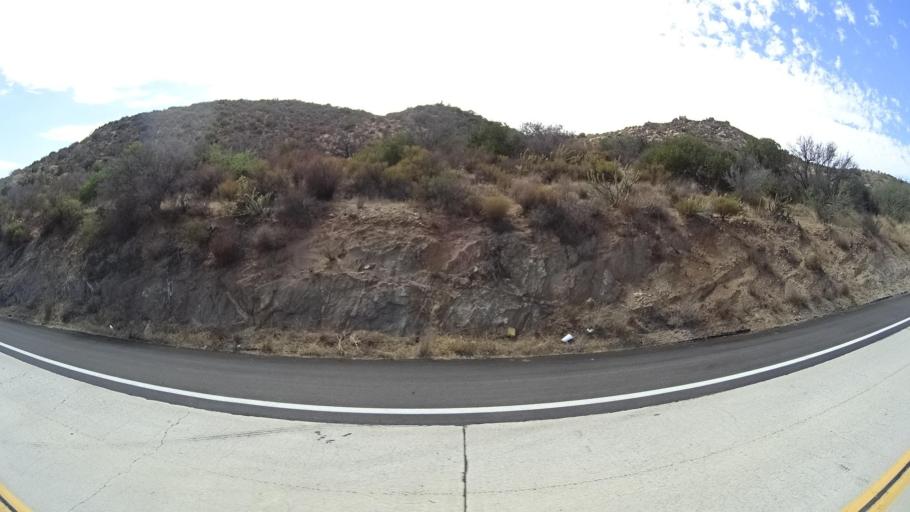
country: MX
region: Baja California
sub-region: Tecate
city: Cereso del Hongo
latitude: 32.6379
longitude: -116.2276
